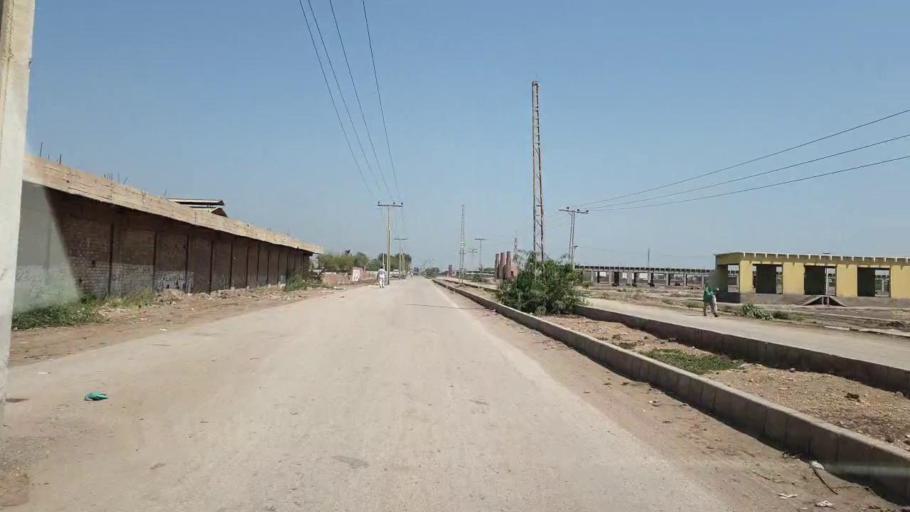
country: PK
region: Sindh
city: Hyderabad
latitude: 25.4179
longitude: 68.3854
